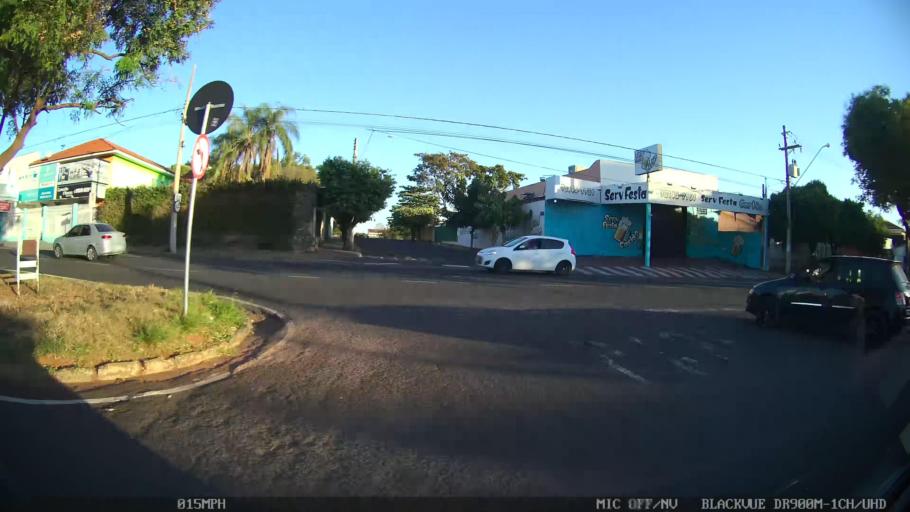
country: BR
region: Sao Paulo
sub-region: Sao Jose Do Rio Preto
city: Sao Jose do Rio Preto
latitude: -20.7795
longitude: -49.3734
